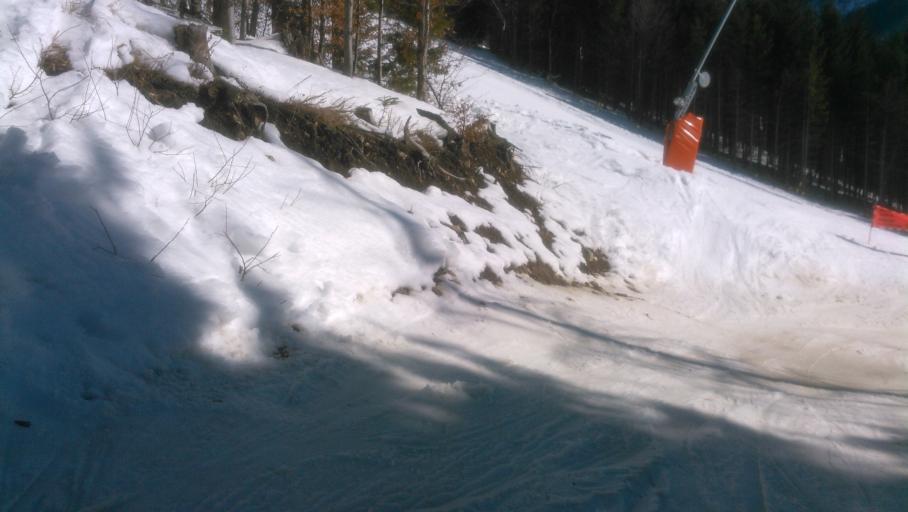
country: SK
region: Banskobystricky
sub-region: Okres Banska Bystrica
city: Brezno
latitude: 48.9253
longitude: 19.5984
